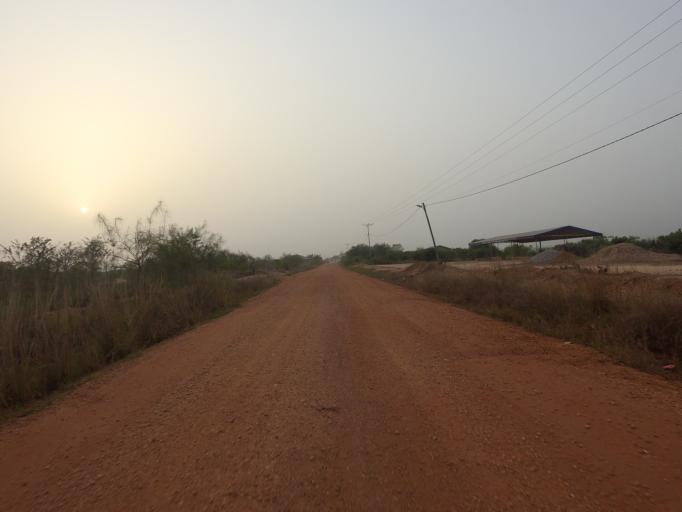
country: GH
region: Volta
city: Anloga
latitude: 5.9718
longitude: 0.6187
